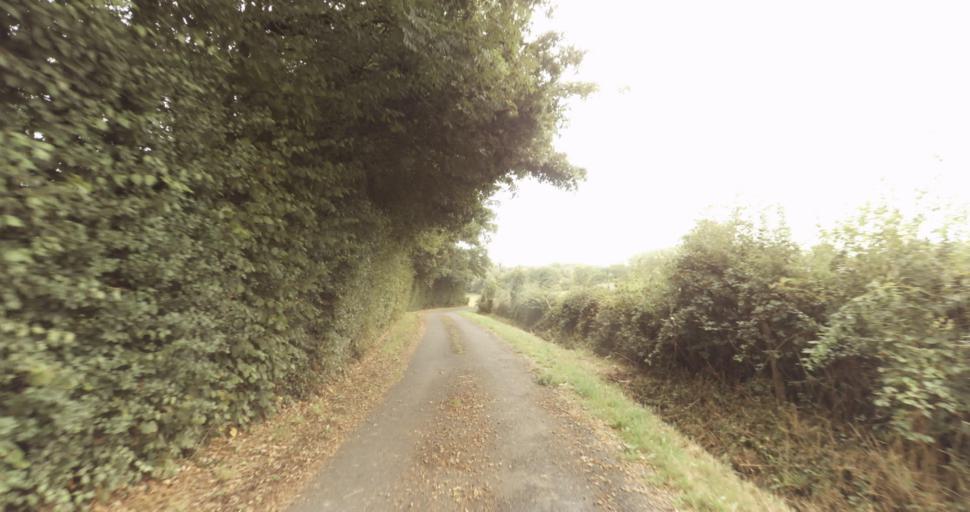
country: FR
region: Lower Normandy
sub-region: Departement de l'Orne
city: Sainte-Gauburge-Sainte-Colombe
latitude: 48.6970
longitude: 0.4443
